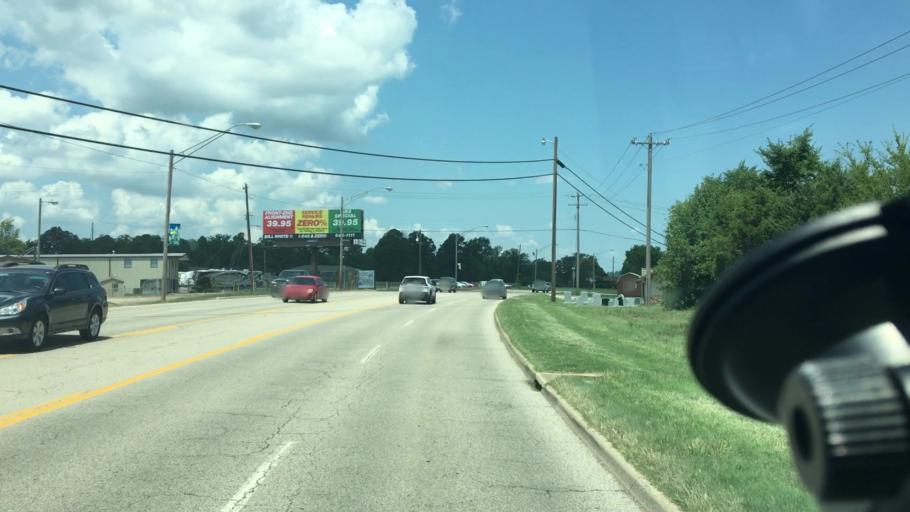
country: US
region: Arkansas
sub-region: Sebastian County
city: Barling
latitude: 35.3366
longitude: -94.3177
